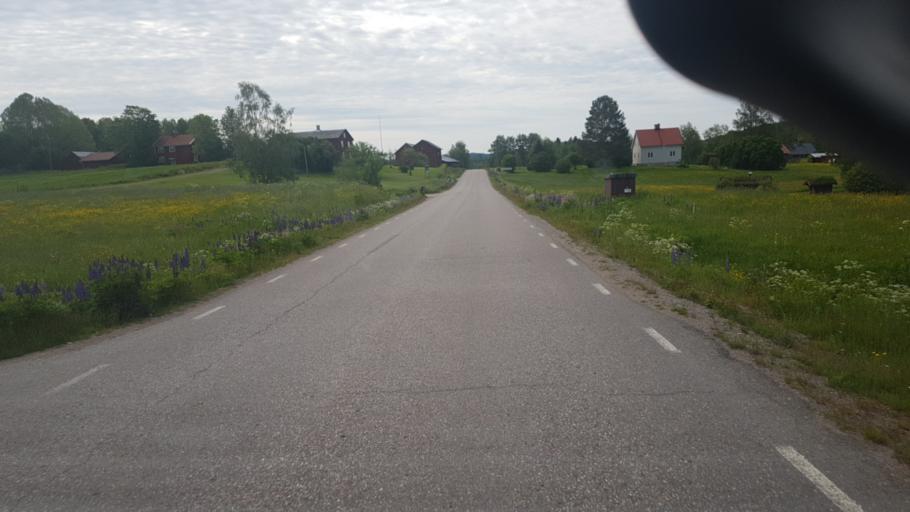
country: SE
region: Vaermland
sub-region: Arvika Kommun
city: Arvika
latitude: 59.7554
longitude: 12.7987
